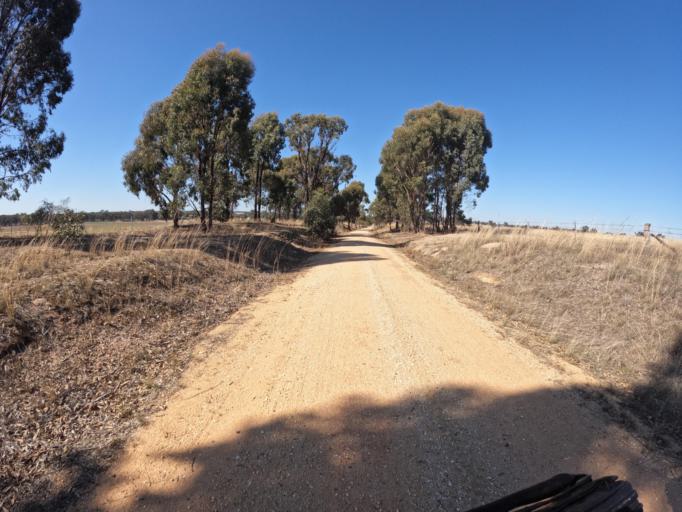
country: AU
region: Victoria
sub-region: Greater Bendigo
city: Kennington
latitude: -36.8208
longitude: 144.5777
